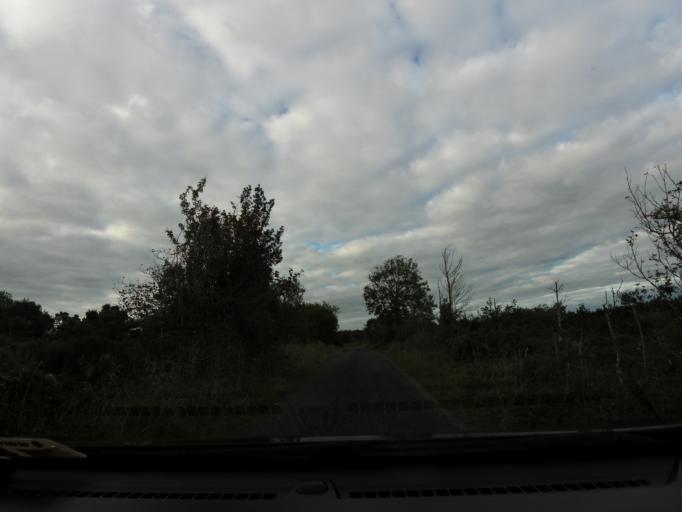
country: IE
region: Connaught
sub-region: County Galway
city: Loughrea
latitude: 53.1307
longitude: -8.5227
